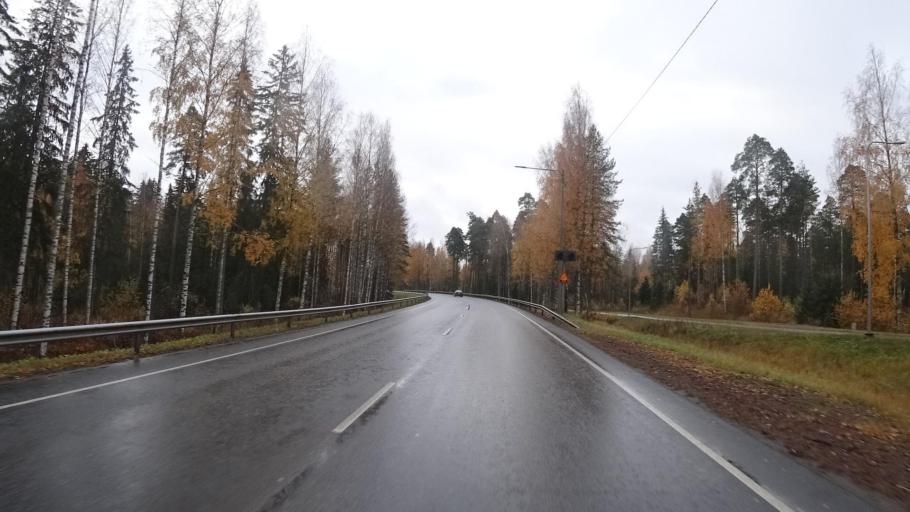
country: FI
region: Northern Savo
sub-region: Varkaus
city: Varkaus
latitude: 62.3066
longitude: 27.9073
